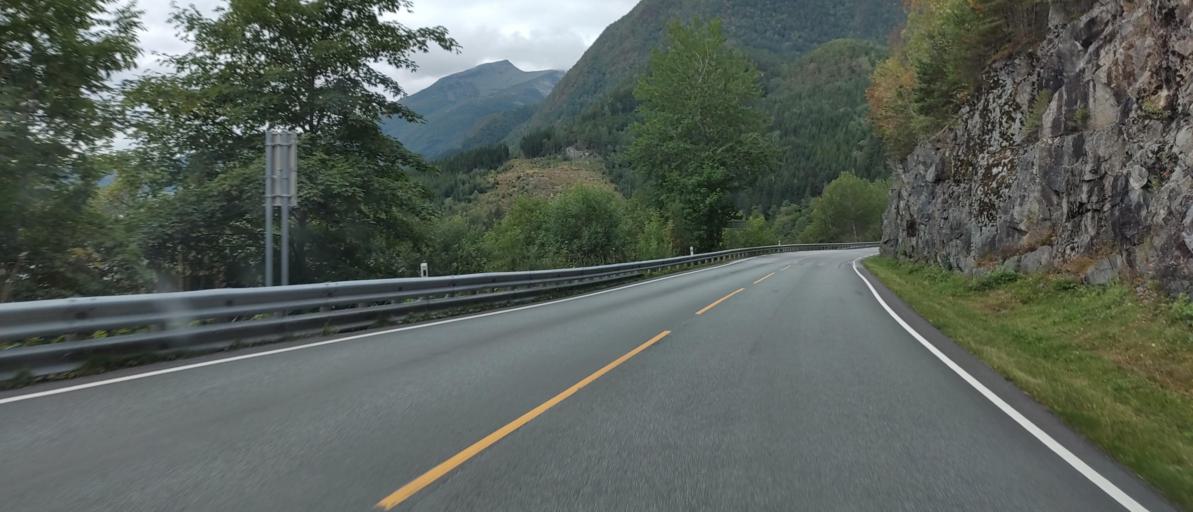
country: NO
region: More og Romsdal
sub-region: Rauma
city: Andalsnes
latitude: 62.5774
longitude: 7.5377
